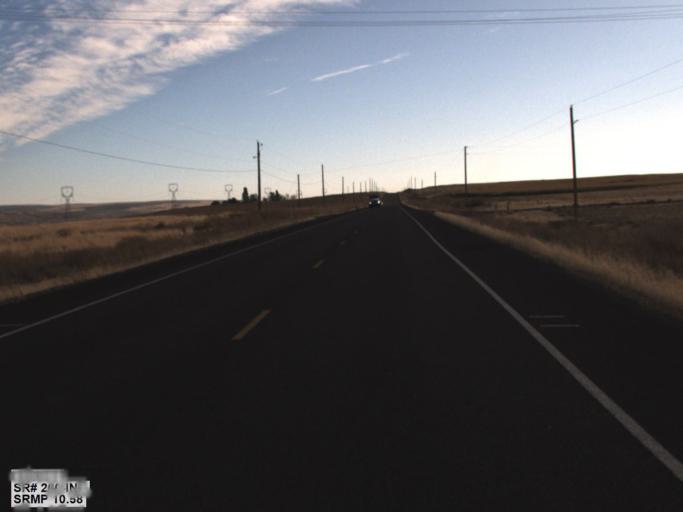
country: US
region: Washington
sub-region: Franklin County
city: Connell
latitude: 46.6347
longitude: -118.7965
